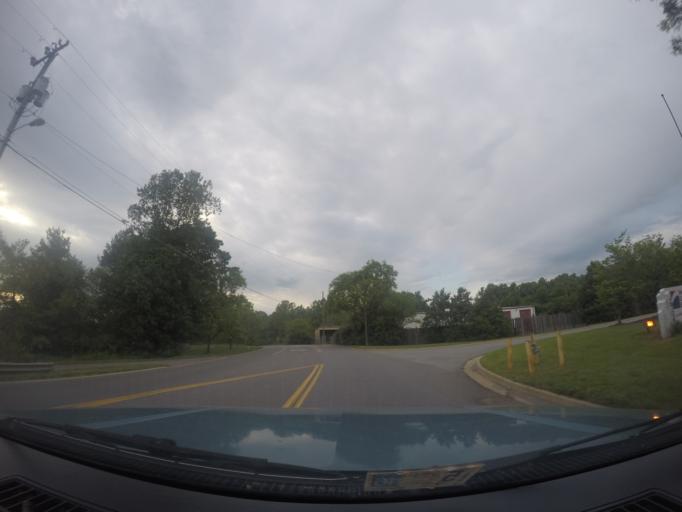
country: US
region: Virginia
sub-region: Amherst County
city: Madison Heights
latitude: 37.3927
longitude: -79.1036
